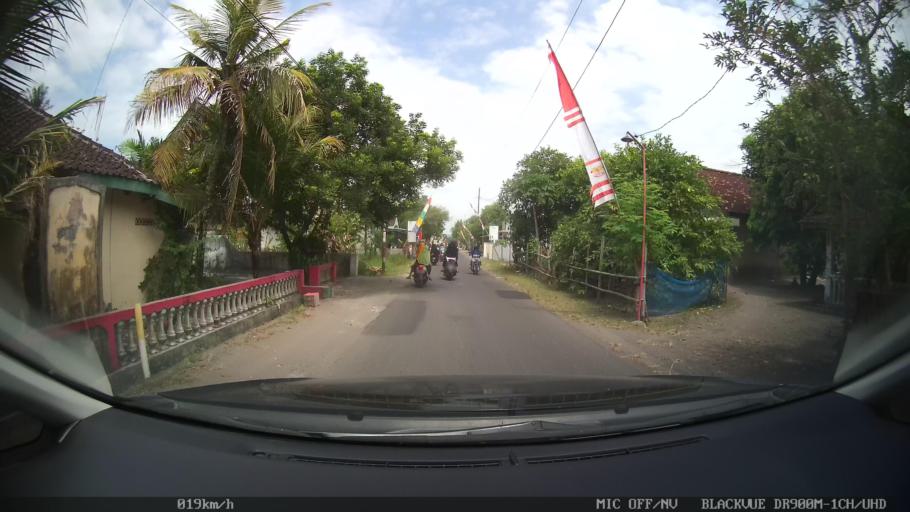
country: ID
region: Central Java
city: Candi Prambanan
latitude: -7.7770
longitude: 110.4774
